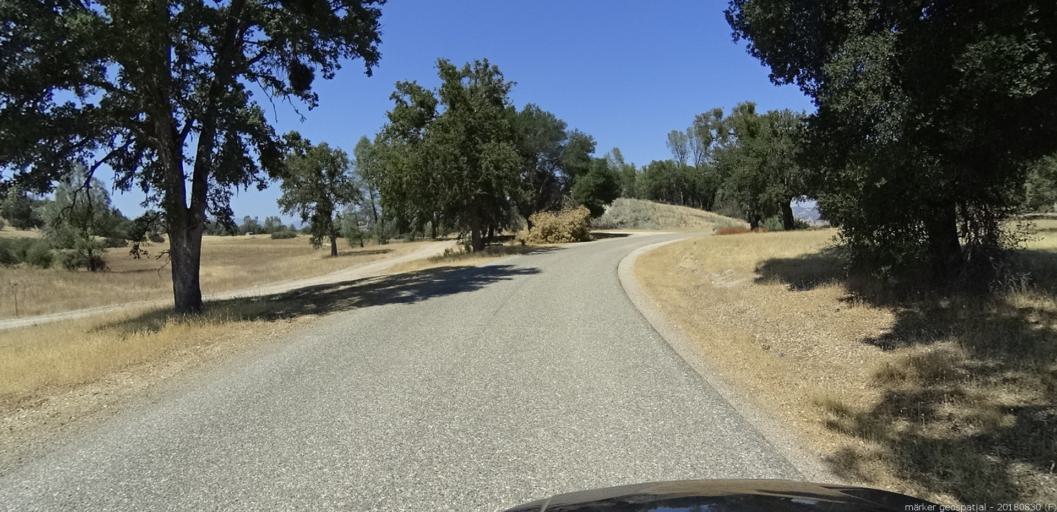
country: US
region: California
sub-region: Monterey County
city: King City
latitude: 35.9931
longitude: -121.2631
